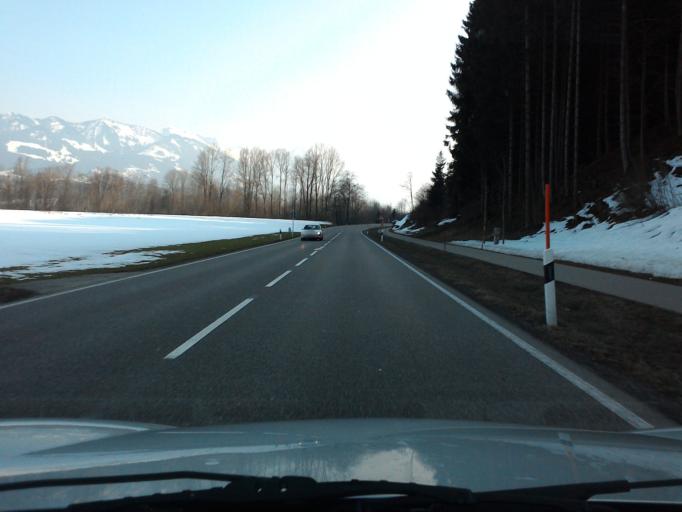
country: DE
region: Bavaria
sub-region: Swabia
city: Sonthofen
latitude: 47.4949
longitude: 10.2659
